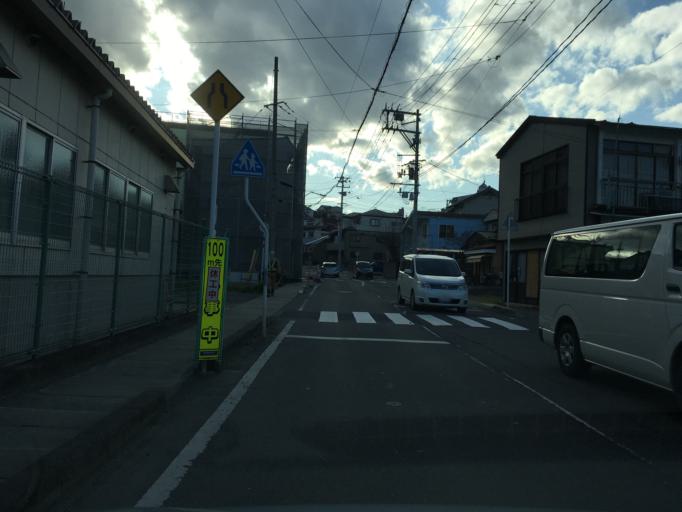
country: JP
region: Miyagi
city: Ishinomaki
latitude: 38.4291
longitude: 141.3049
